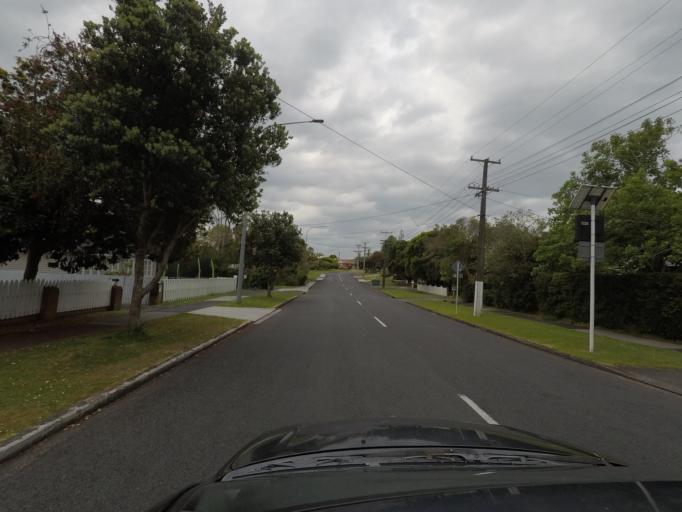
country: NZ
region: Auckland
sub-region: Auckland
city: Rosebank
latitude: -36.8487
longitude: 174.6459
